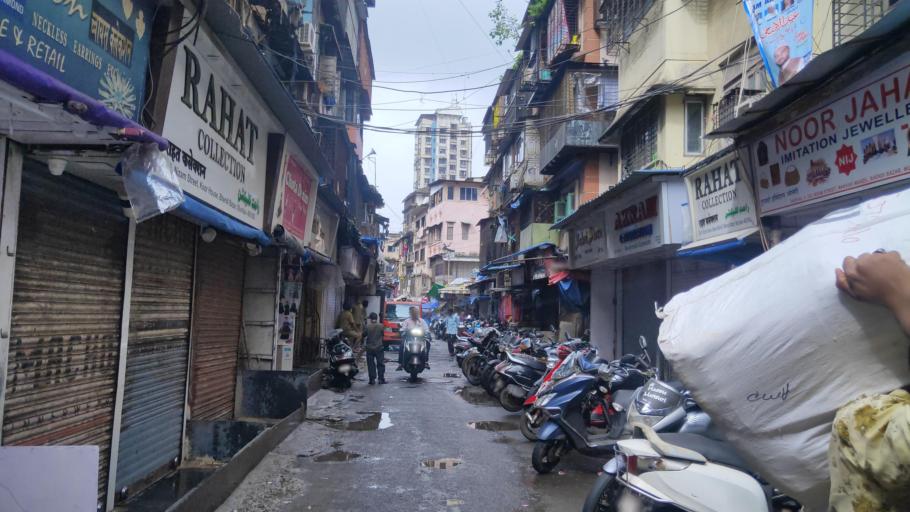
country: IN
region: Maharashtra
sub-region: Mumbai Suburban
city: Mumbai
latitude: 18.9578
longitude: 72.8318
